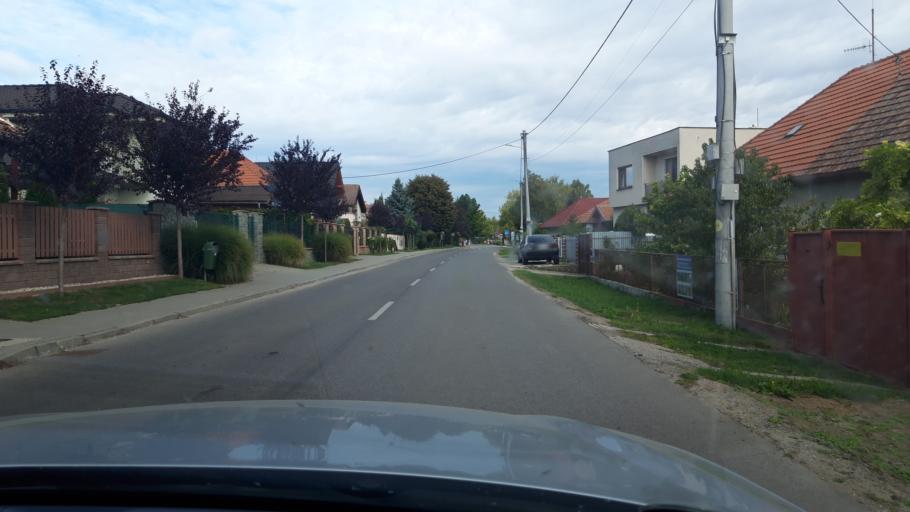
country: SK
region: Nitriansky
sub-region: Okres Nitra
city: Vrable
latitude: 48.1032
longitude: 18.3372
